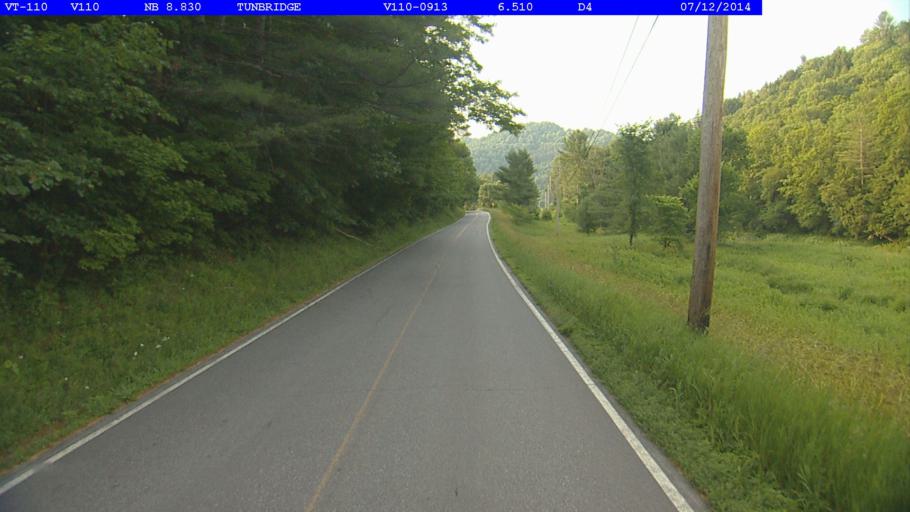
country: US
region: Vermont
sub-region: Orange County
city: Chelsea
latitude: 43.9333
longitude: -72.4663
